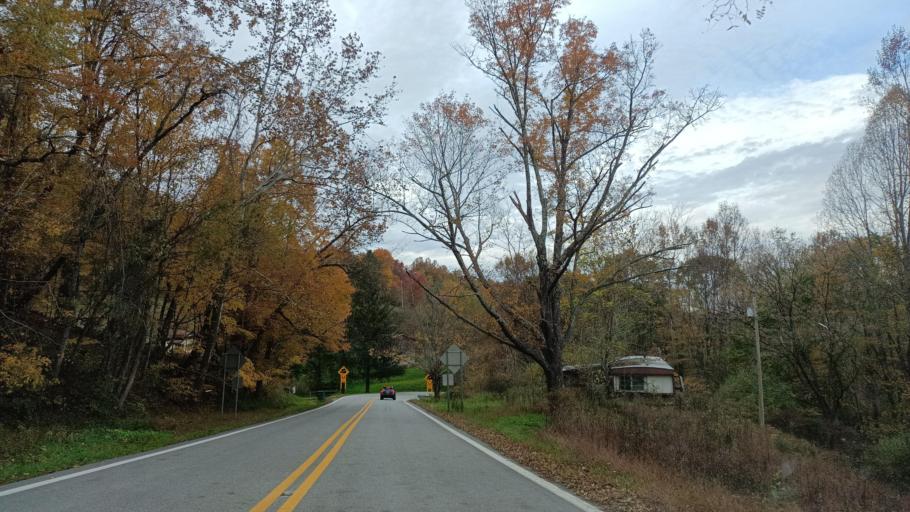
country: US
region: West Virginia
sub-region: Taylor County
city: Grafton
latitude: 39.3322
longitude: -79.9312
